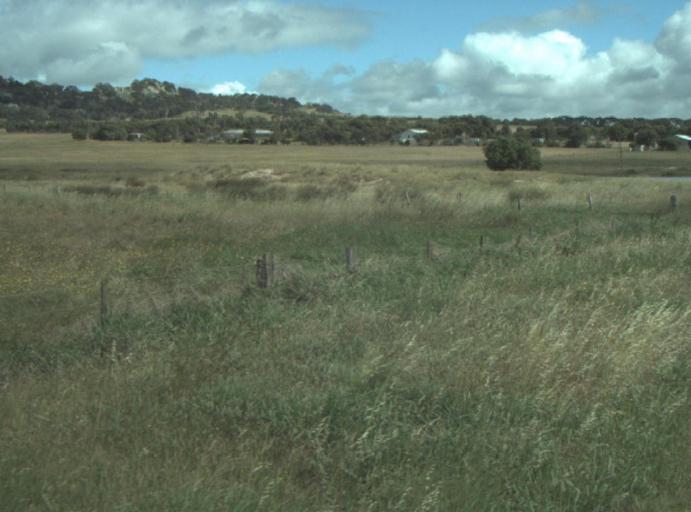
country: AU
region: Victoria
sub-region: Greater Geelong
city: Lara
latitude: -37.8830
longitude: 144.3209
